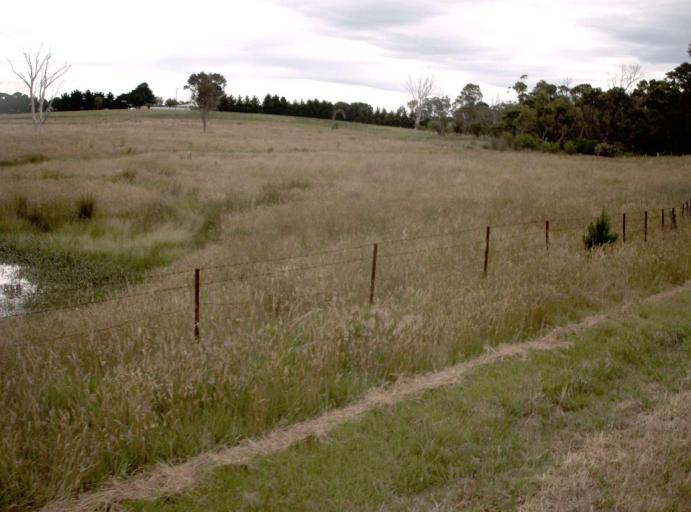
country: AU
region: Victoria
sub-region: East Gippsland
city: Bairnsdale
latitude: -37.9762
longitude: 147.4646
